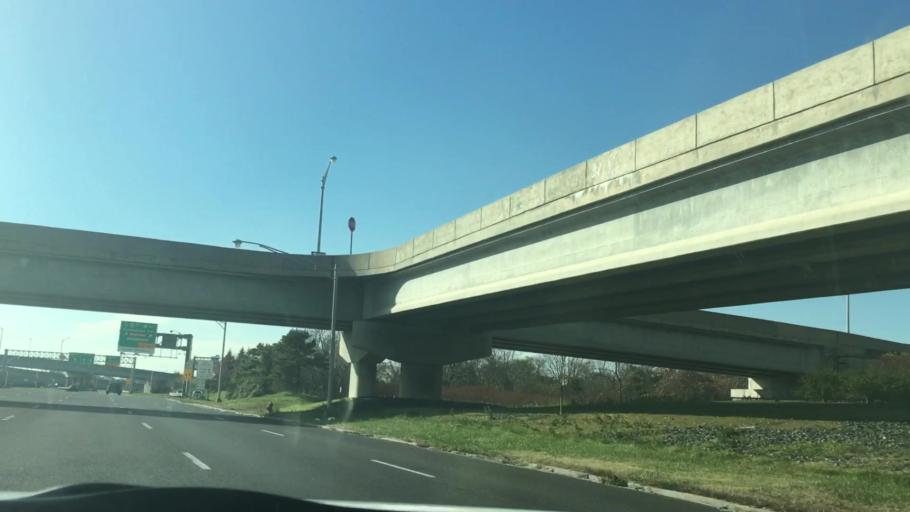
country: US
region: New Jersey
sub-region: Atlantic County
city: Atlantic City
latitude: 39.3754
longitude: -74.4366
